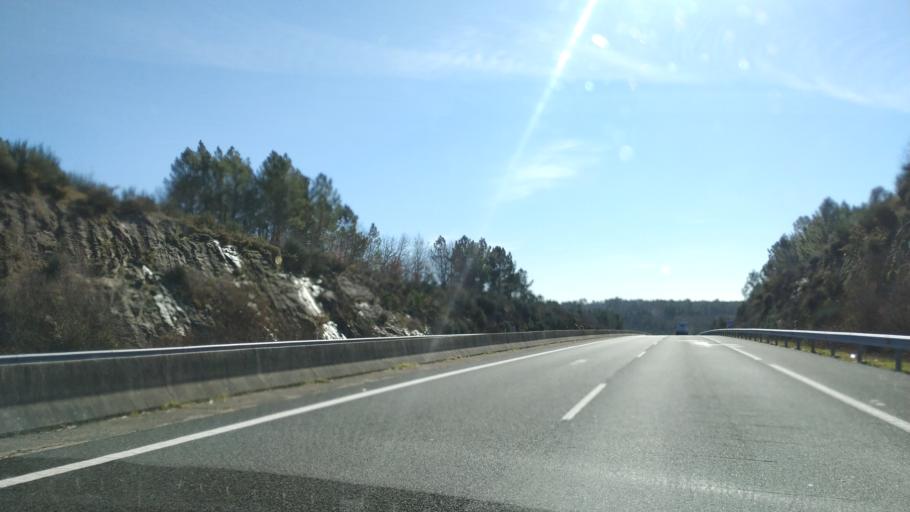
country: ES
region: Galicia
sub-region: Provincia de Ourense
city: Pinor
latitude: 42.4896
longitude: -8.0237
